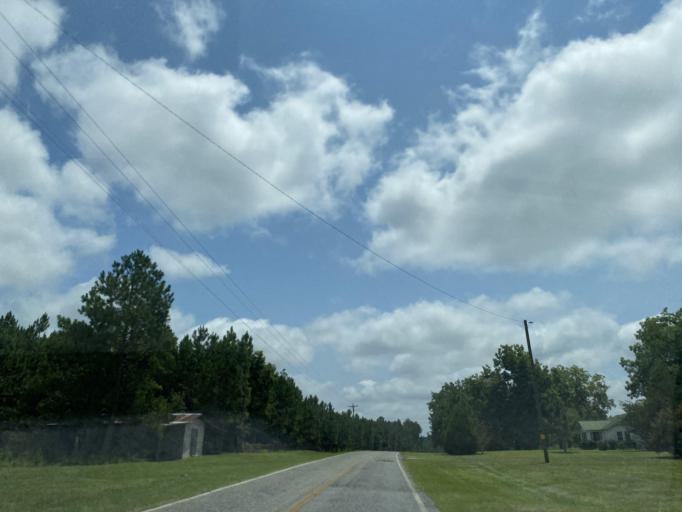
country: US
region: Georgia
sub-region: Wheeler County
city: Alamo
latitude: 32.1088
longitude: -82.7767
